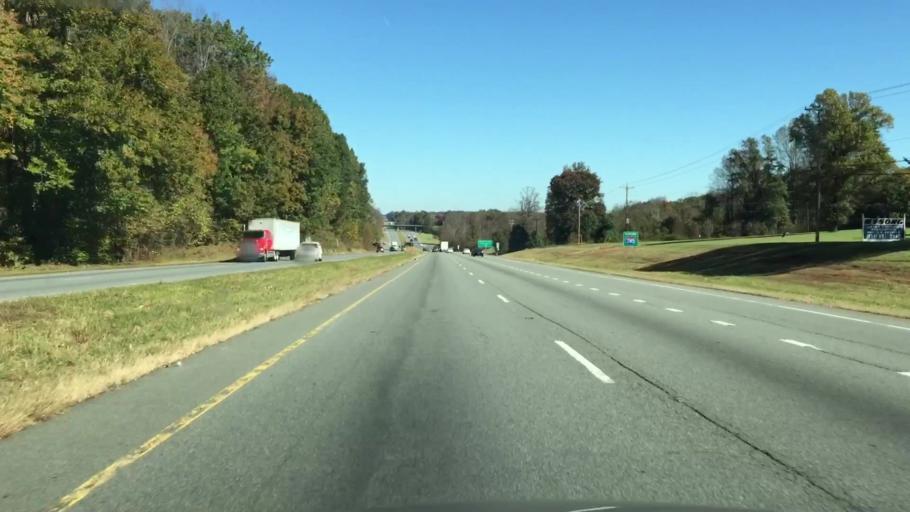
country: US
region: North Carolina
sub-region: Guilford County
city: McLeansville
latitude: 36.1680
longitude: -79.7171
